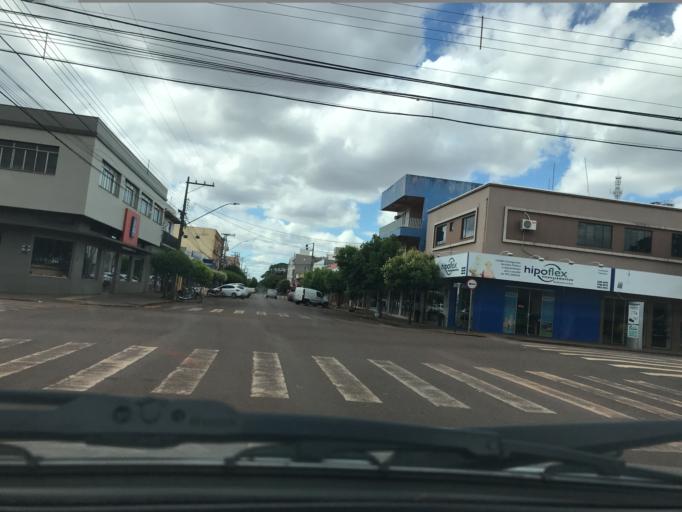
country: BR
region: Parana
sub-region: Palotina
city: Palotina
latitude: -24.2842
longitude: -53.8384
